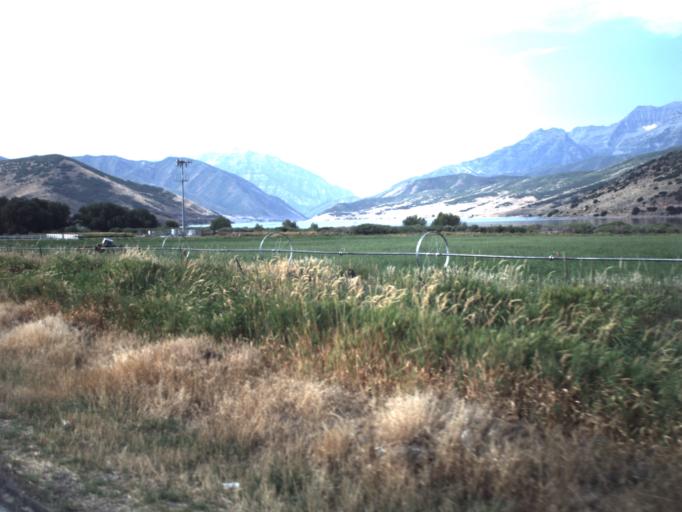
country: US
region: Utah
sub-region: Wasatch County
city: Midway
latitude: 40.4656
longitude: -111.4718
